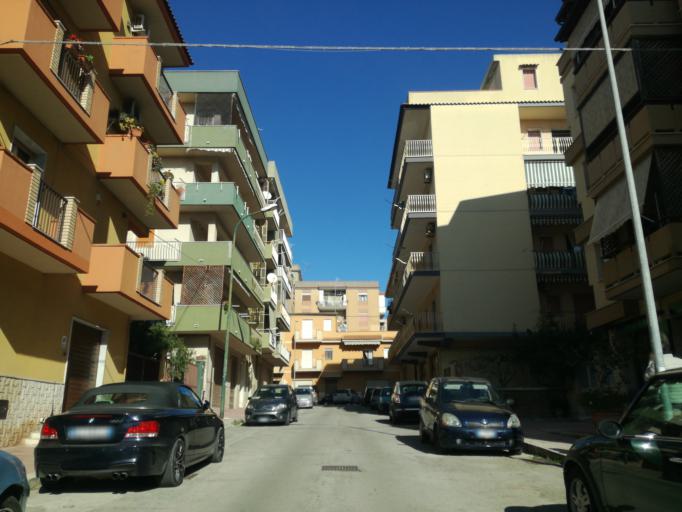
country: IT
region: Sicily
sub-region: Provincia di Caltanissetta
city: Gela
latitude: 37.0723
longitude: 14.2325
